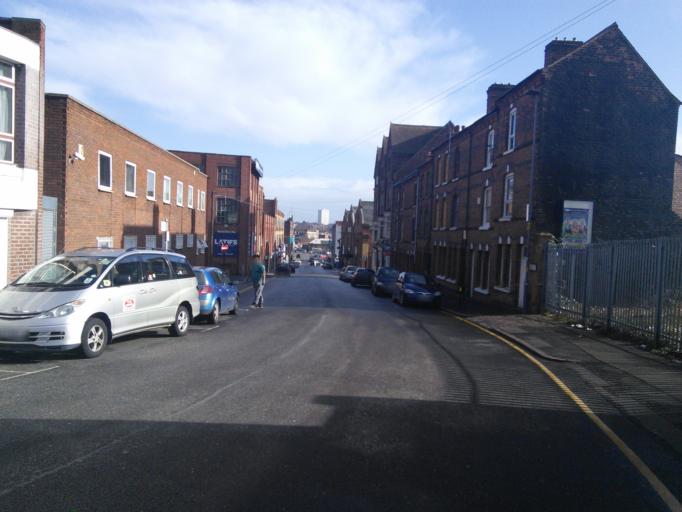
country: GB
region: England
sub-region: City and Borough of Birmingham
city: Birmingham
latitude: 52.4790
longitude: -1.8902
